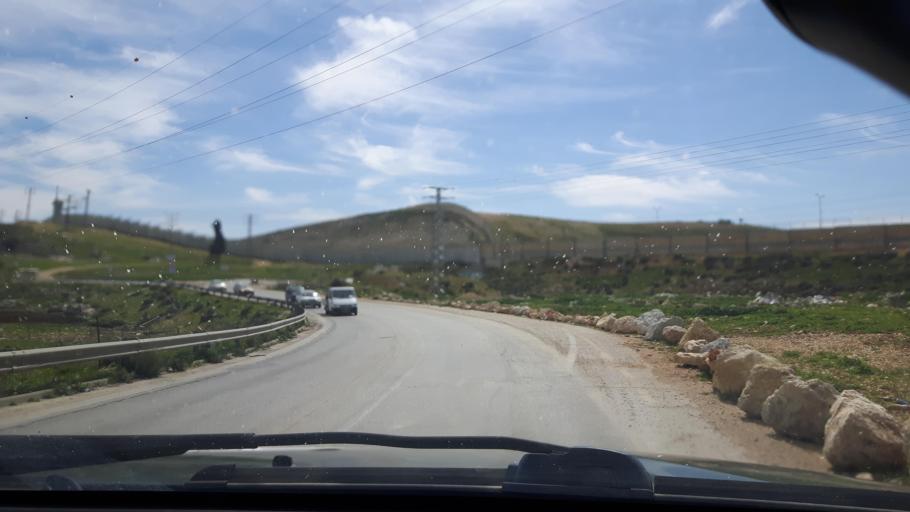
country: PS
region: West Bank
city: Qalandiya
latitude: 31.8620
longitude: 35.2036
